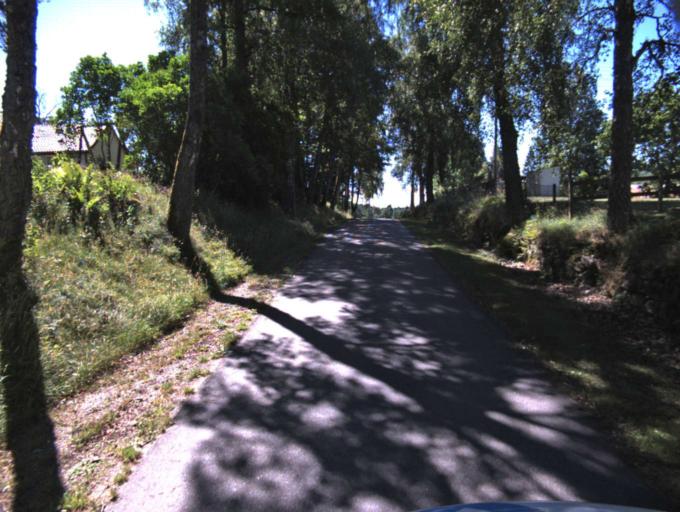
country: SE
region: Vaestra Goetaland
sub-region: Ulricehamns Kommun
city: Ulricehamn
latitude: 57.6626
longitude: 13.4306
